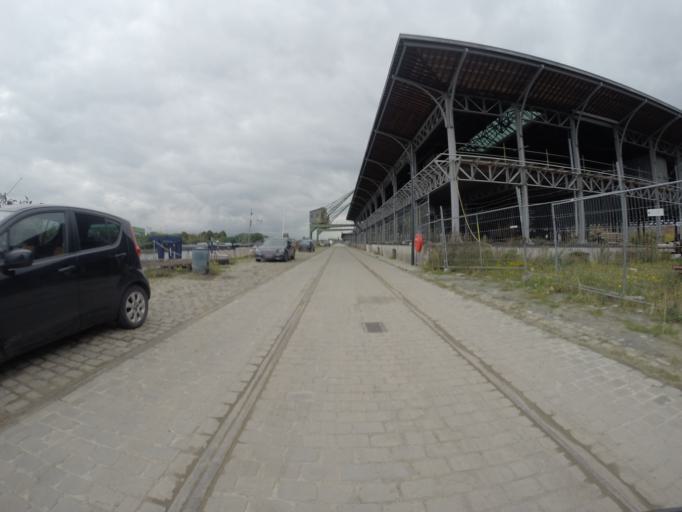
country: BE
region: Flanders
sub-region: Provincie Oost-Vlaanderen
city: Gent
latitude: 51.0743
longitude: 3.7277
